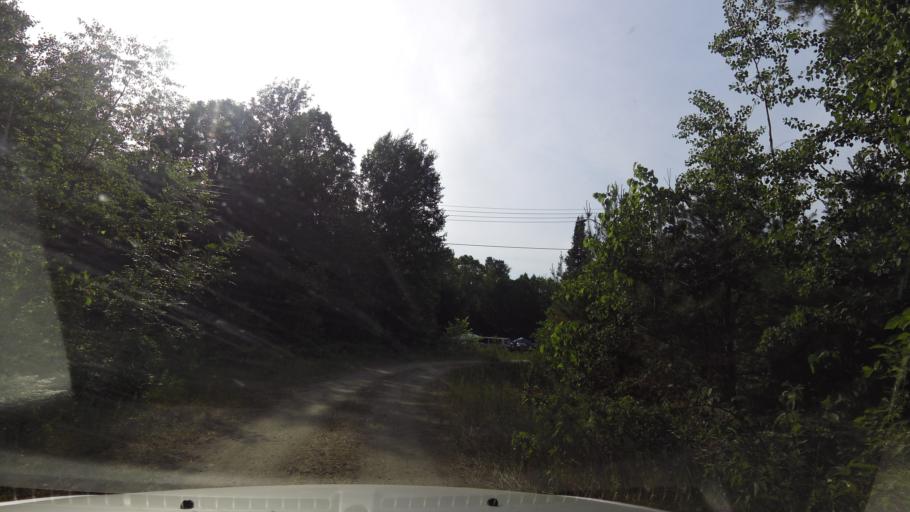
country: CA
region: Ontario
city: Greater Sudbury
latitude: 45.9087
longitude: -80.5553
